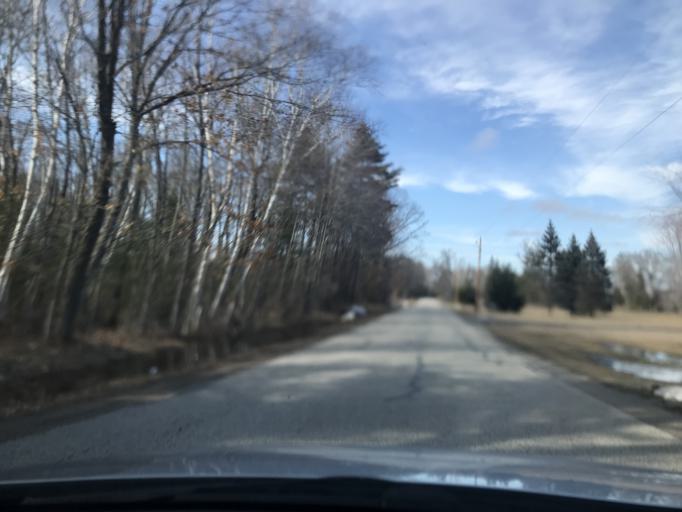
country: US
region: Wisconsin
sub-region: Marinette County
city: Marinette
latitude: 45.0389
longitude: -87.6677
